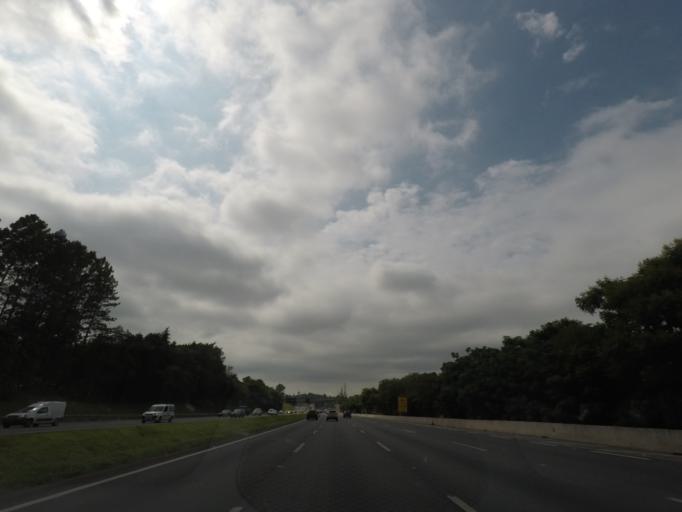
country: BR
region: Sao Paulo
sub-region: Campinas
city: Campinas
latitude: -22.8908
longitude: -47.0105
